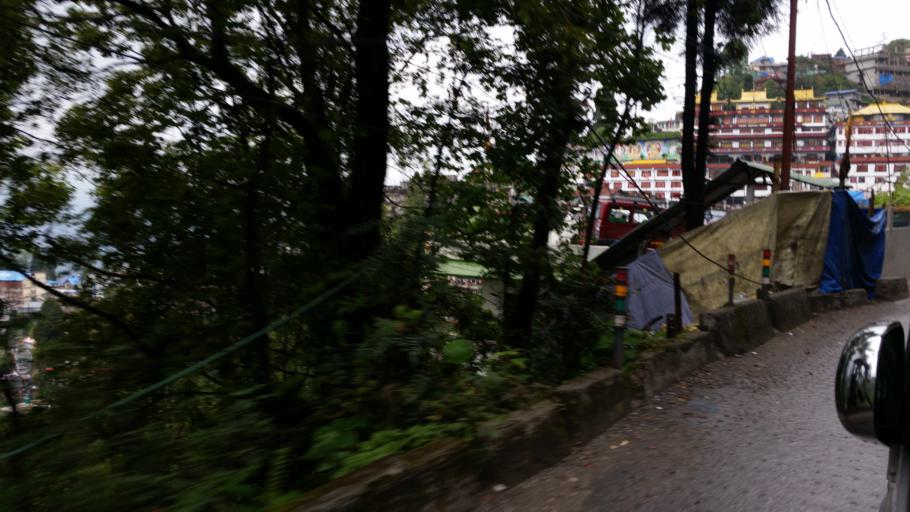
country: IN
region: West Bengal
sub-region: Darjiling
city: Darjiling
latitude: 27.0219
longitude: 88.2539
